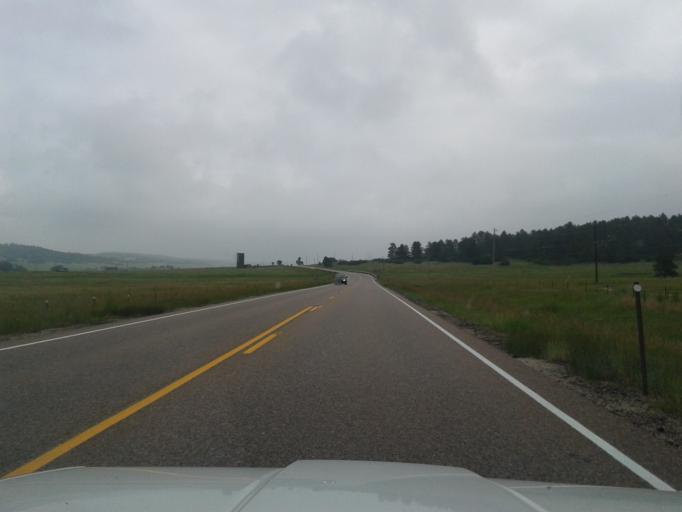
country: US
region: Colorado
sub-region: El Paso County
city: Woodmoor
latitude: 39.1792
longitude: -104.7350
